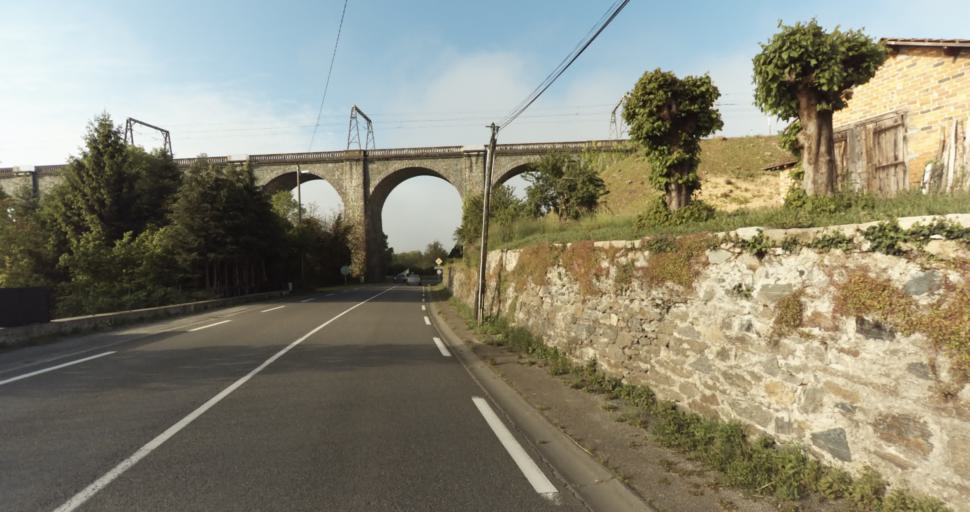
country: FR
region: Limousin
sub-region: Departement de la Haute-Vienne
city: Le Vigen
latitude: 45.7553
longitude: 1.2907
